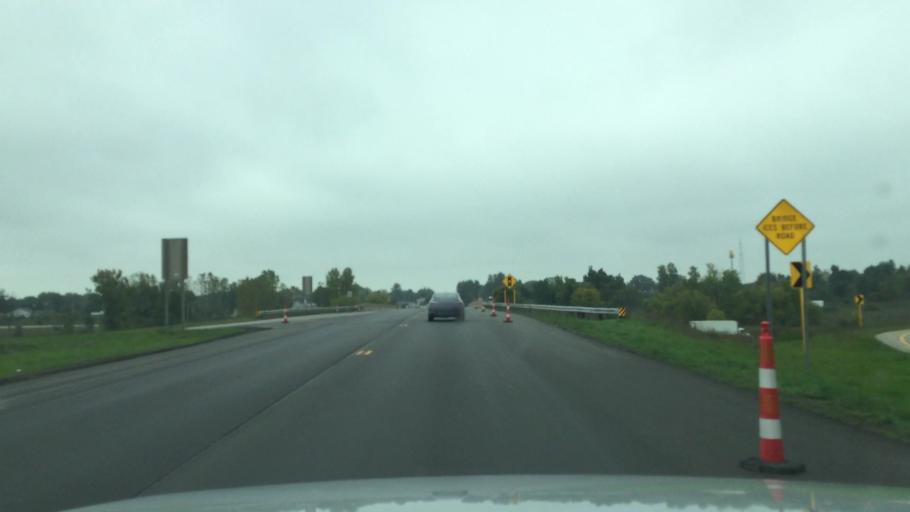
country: US
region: Michigan
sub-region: Shiawassee County
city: Perry
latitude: 42.8415
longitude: -84.2200
